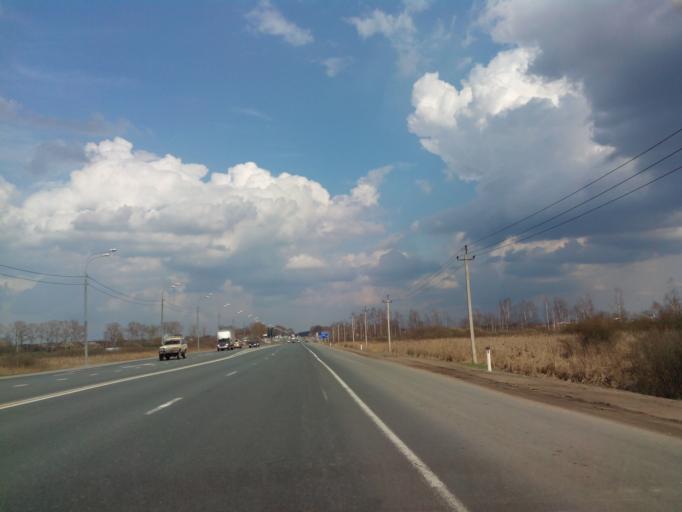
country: RU
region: Moskovskaya
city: Chupryakovo
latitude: 55.5570
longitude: 36.5594
